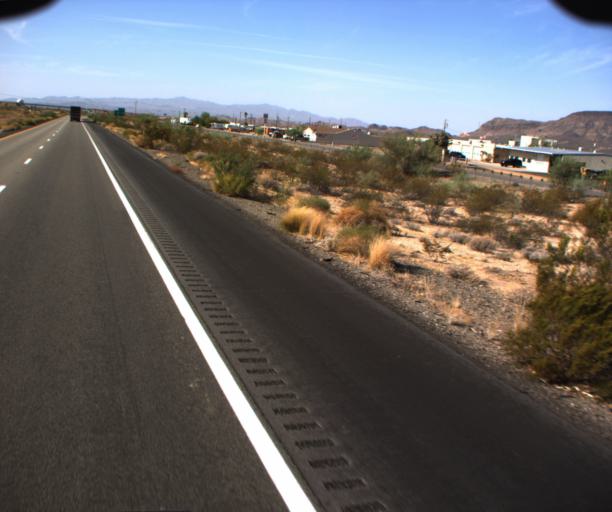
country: US
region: Arizona
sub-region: Mohave County
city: Kingman
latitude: 34.8712
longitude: -114.1478
